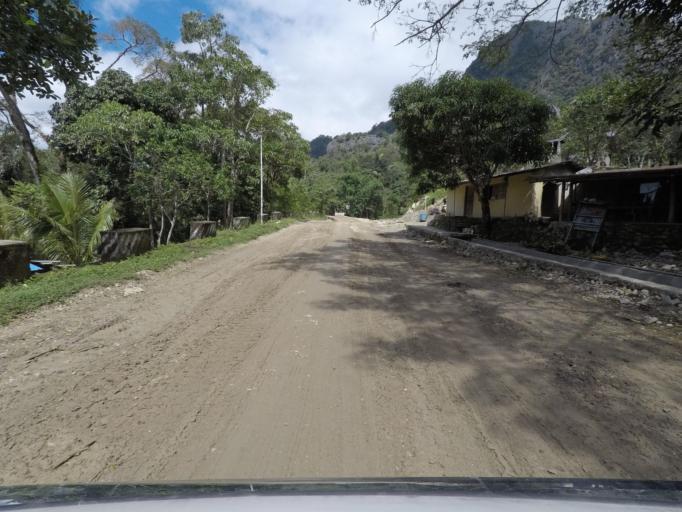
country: TL
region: Baucau
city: Venilale
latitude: -8.7224
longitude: 126.3670
